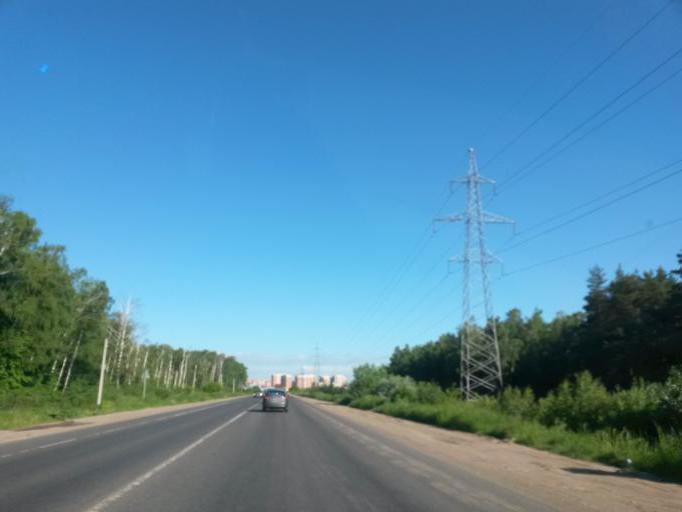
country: RU
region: Moskovskaya
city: Shcherbinka
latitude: 55.4913
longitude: 37.5899
